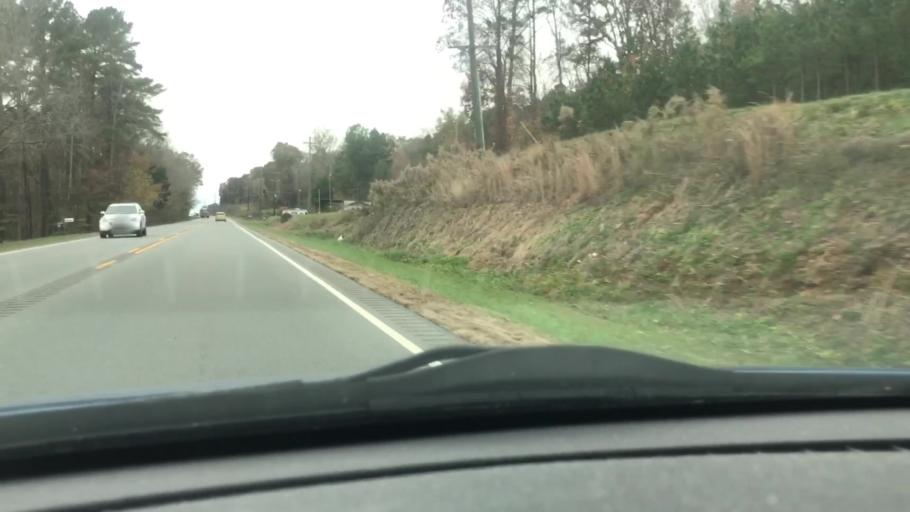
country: US
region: North Carolina
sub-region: Davidson County
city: Thomasville
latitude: 35.7628
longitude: -80.0677
